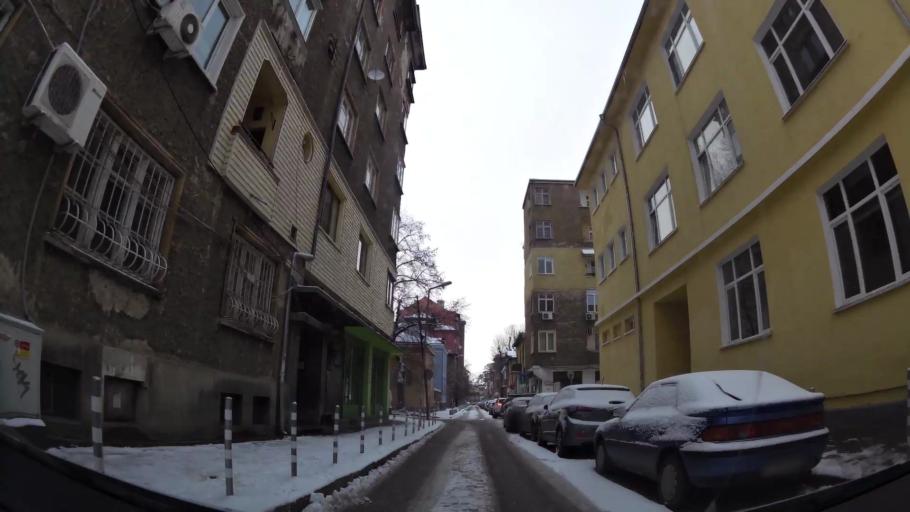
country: BG
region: Sofia-Capital
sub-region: Stolichna Obshtina
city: Sofia
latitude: 42.7003
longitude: 23.3285
